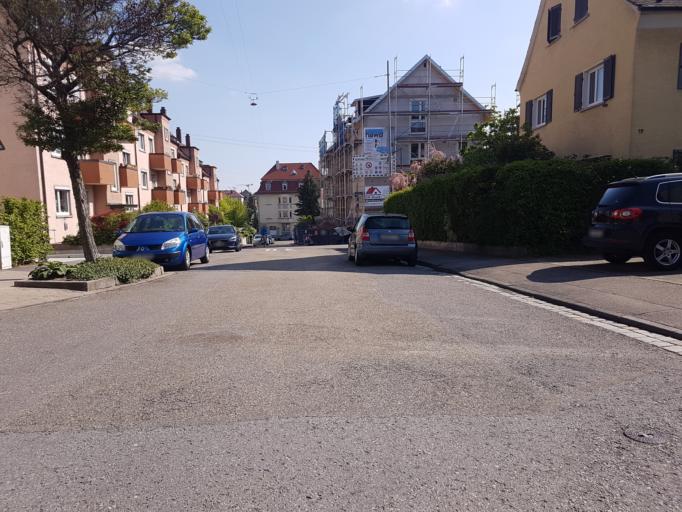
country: DE
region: Baden-Wuerttemberg
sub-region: Regierungsbezirk Stuttgart
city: Ludwigsburg
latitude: 48.8962
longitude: 9.1740
